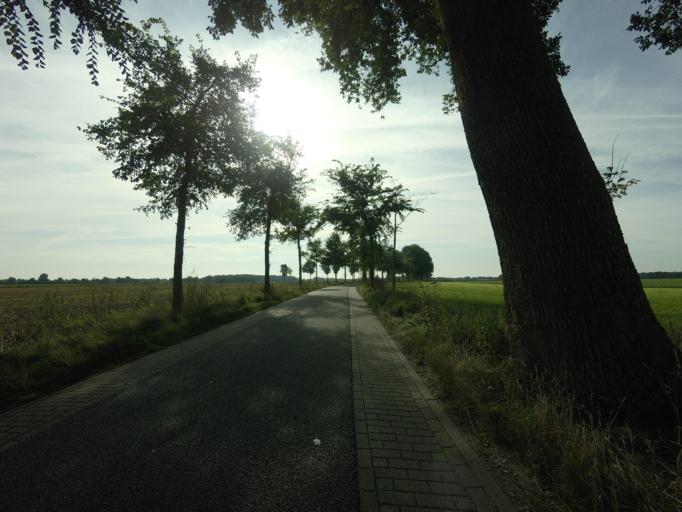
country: NL
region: Drenthe
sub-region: Gemeente Assen
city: Assen
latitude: 53.0055
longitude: 6.6209
